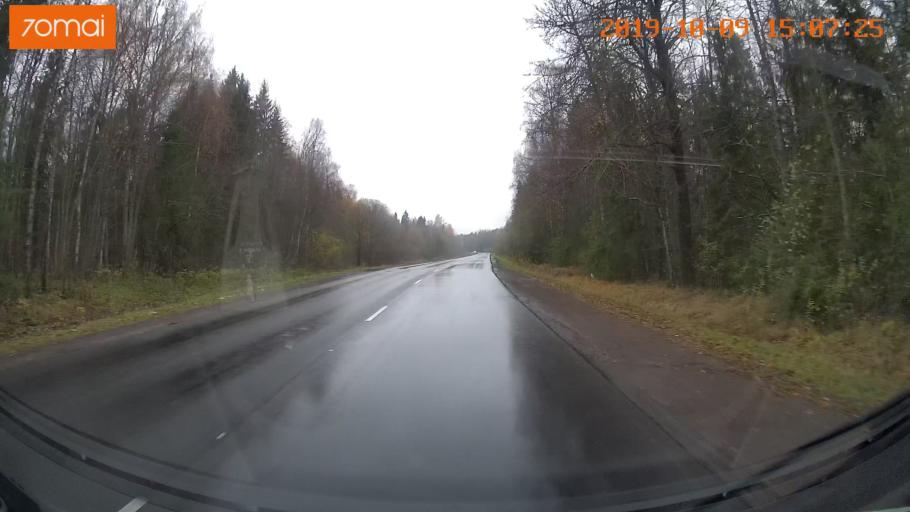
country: RU
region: Kostroma
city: Susanino
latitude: 58.2195
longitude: 41.6504
